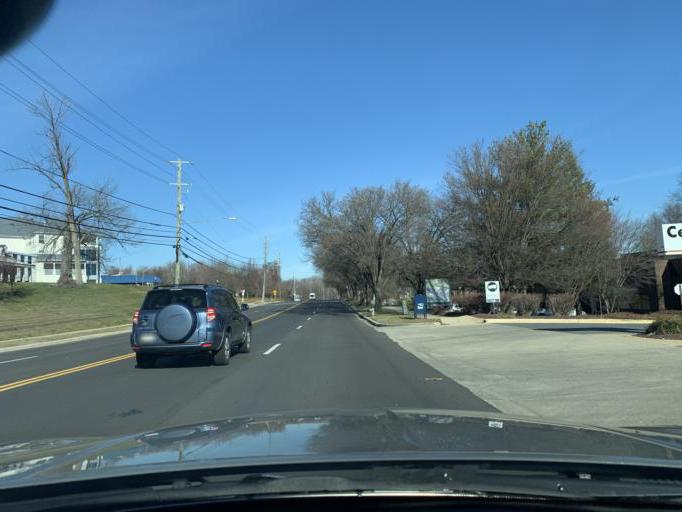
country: US
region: Maryland
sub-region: Prince George's County
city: Largo
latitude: 38.9023
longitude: -76.8532
